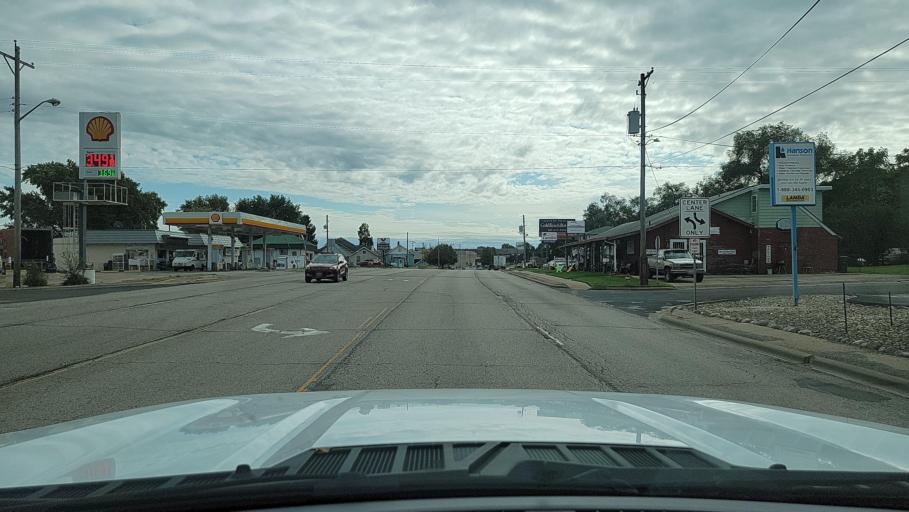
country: US
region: Illinois
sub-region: Peoria County
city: Bartonville
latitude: 40.6489
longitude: -89.6497
